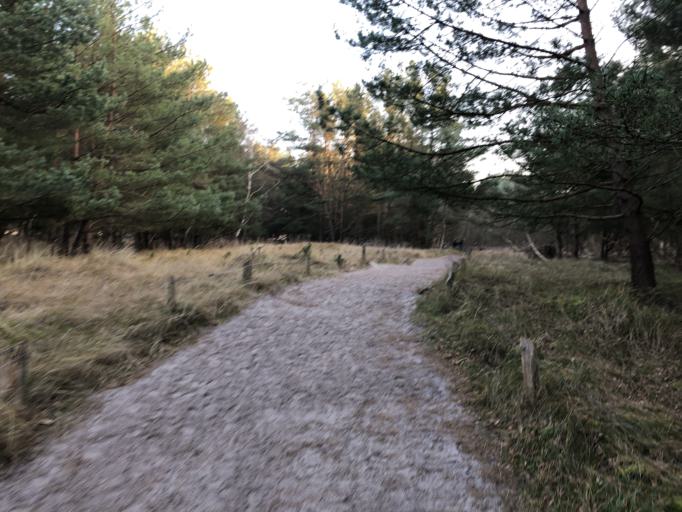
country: DE
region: Mecklenburg-Vorpommern
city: Ostseebad Prerow
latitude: 54.4706
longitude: 12.5190
